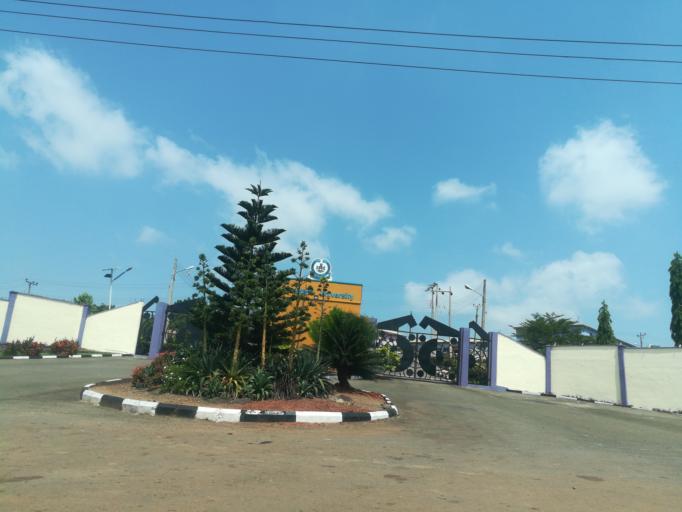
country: NG
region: Ogun
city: Abeokuta
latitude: 7.1405
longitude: 3.3984
